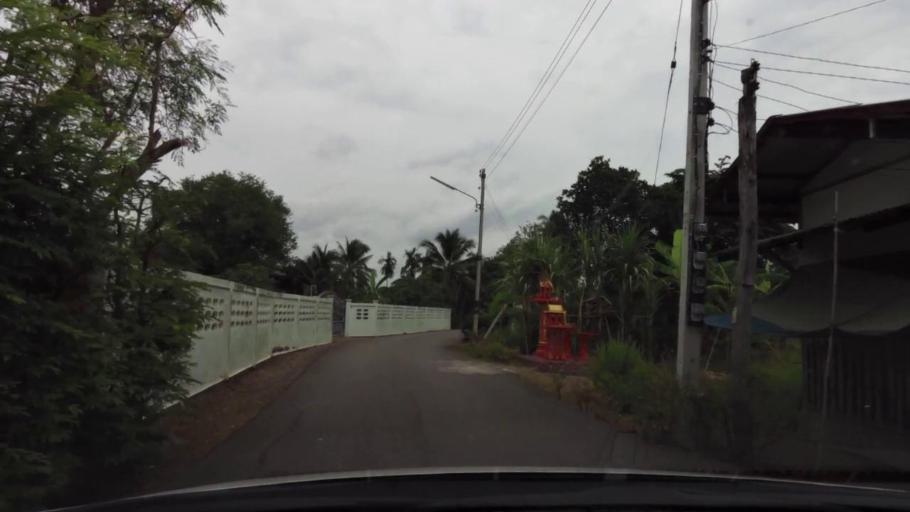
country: TH
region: Samut Sakhon
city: Ban Phaeo
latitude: 13.5960
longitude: 100.0295
